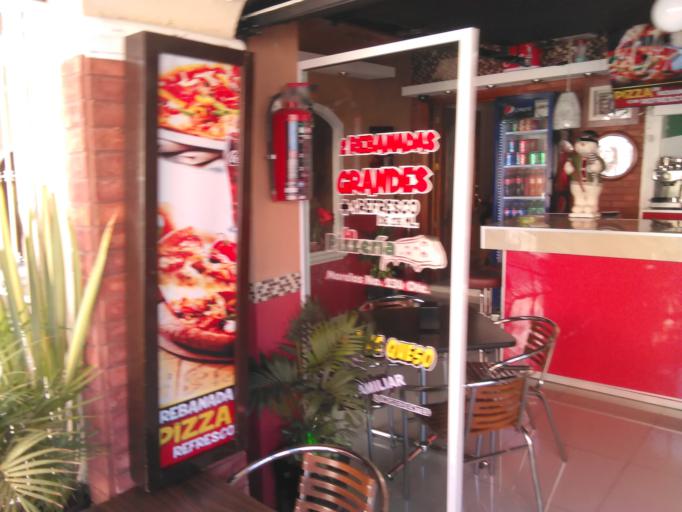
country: MX
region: Nayarit
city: Tepic
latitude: 21.5078
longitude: -104.8886
